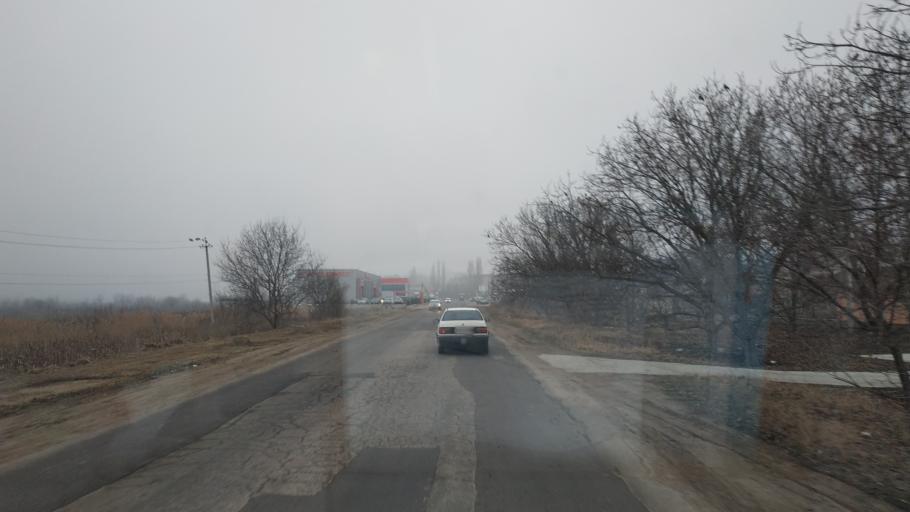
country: MD
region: Laloveni
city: Ialoveni
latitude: 46.9487
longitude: 28.7687
